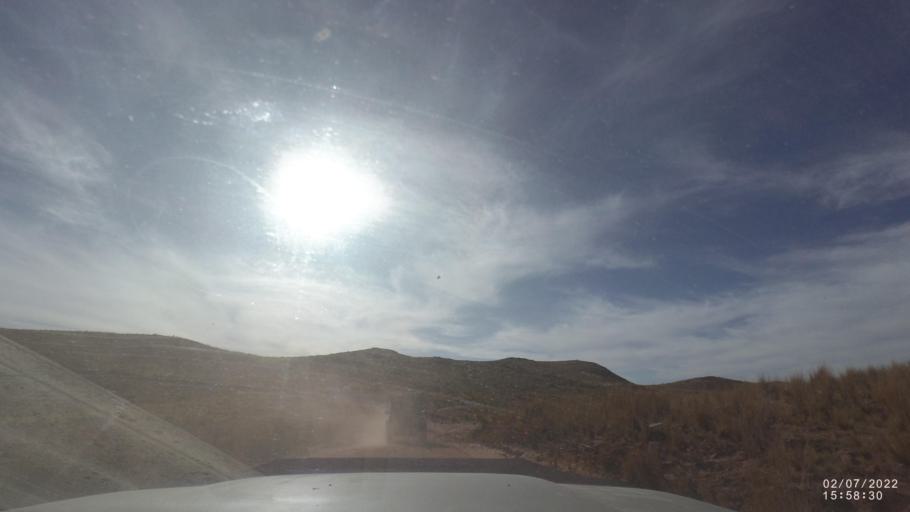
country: BO
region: Cochabamba
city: Irpa Irpa
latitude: -17.9064
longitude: -66.4319
